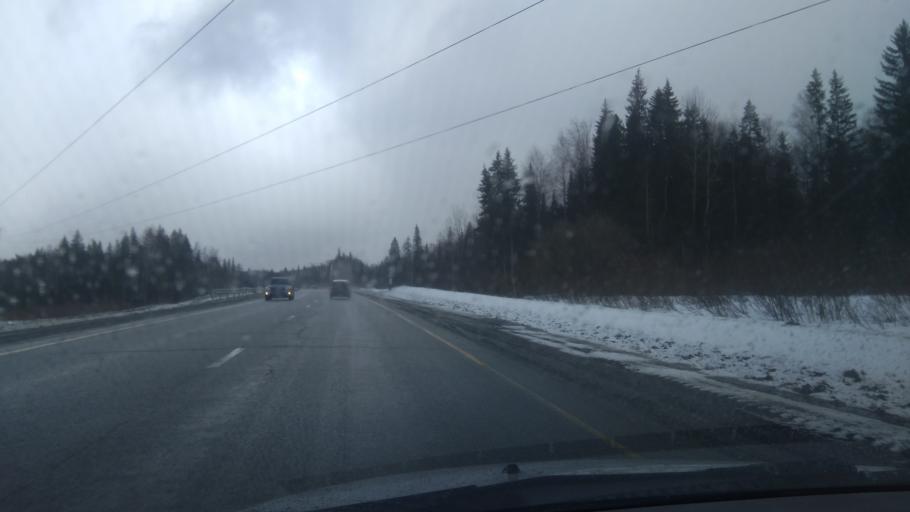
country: RU
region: Sverdlovsk
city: Arti
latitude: 56.7865
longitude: 58.5173
